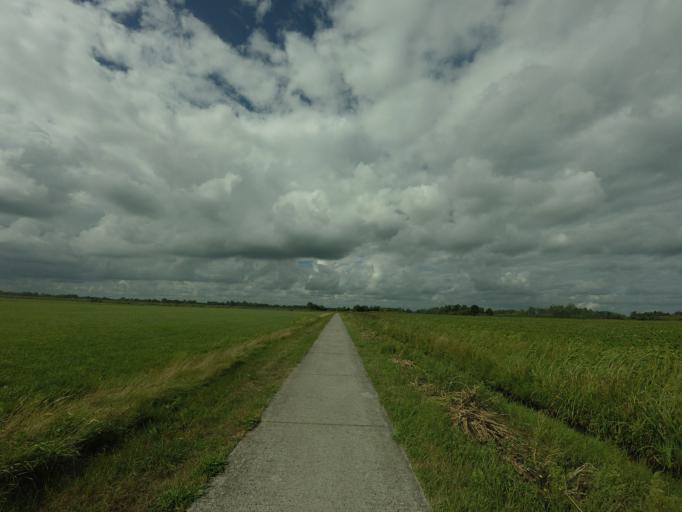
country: NL
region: Overijssel
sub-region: Gemeente Steenwijkerland
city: Wanneperveen
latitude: 52.7081
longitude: 6.1028
